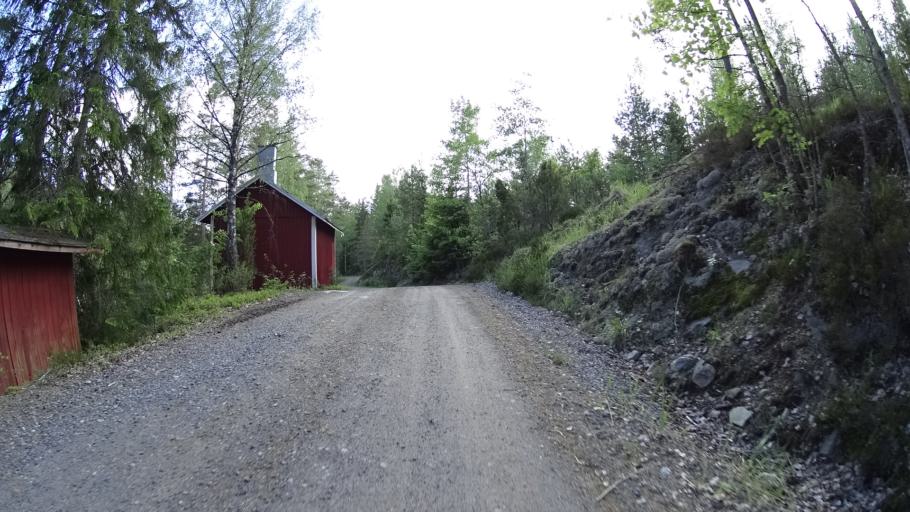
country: FI
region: Varsinais-Suomi
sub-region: Salo
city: Kisko
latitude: 60.1650
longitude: 23.4912
